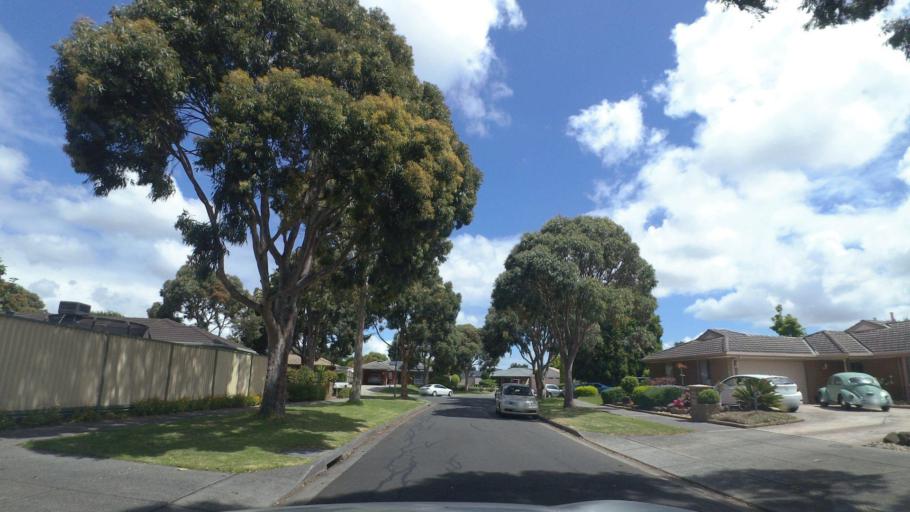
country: AU
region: Victoria
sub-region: Knox
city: Ferntree Gully
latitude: -37.8955
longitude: 145.2772
